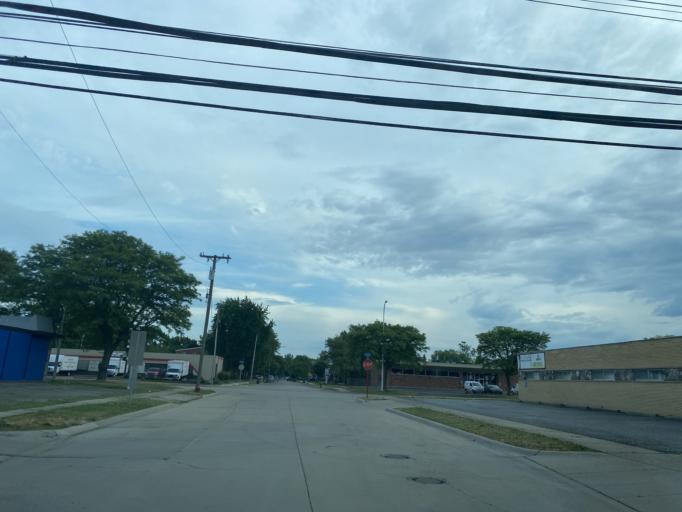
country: US
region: Michigan
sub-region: Wayne County
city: Allen Park
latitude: 42.2568
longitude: -83.2396
